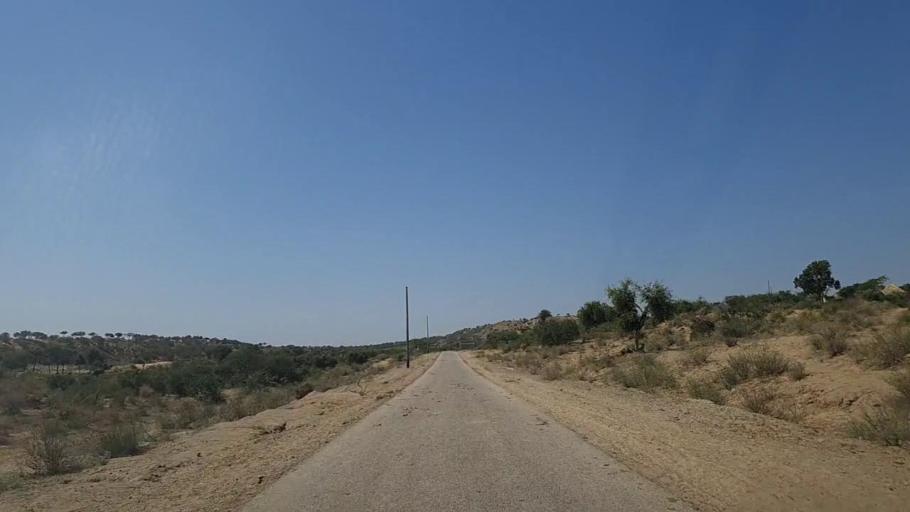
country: PK
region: Sindh
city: Mithi
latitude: 24.7861
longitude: 69.7662
